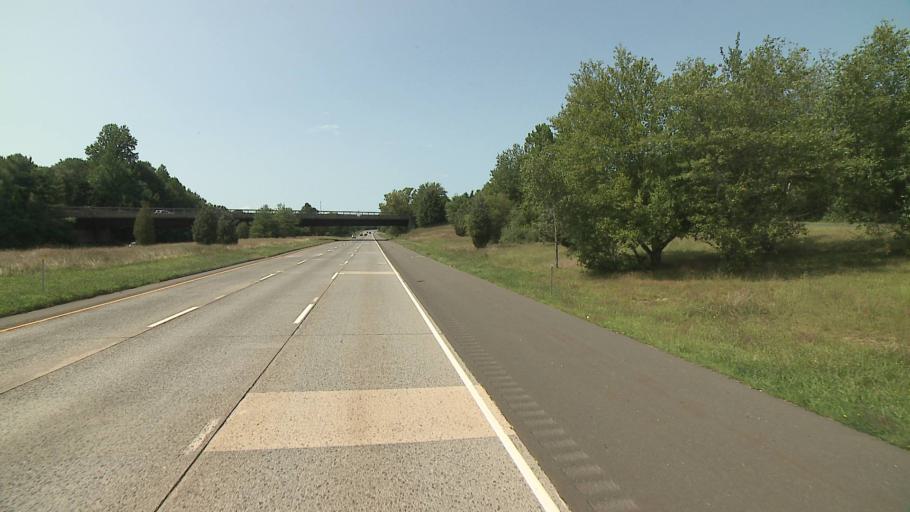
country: US
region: Connecticut
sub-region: Fairfield County
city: Trumbull
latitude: 41.2518
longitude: -73.1960
